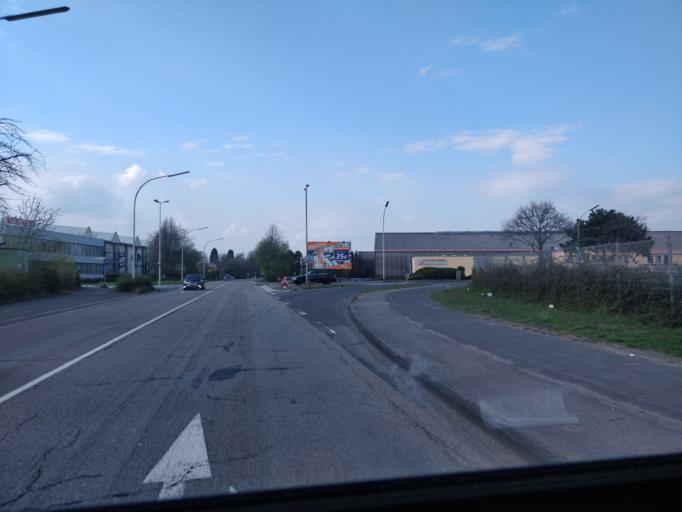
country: DE
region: North Rhine-Westphalia
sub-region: Regierungsbezirk Koln
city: Frechen
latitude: 50.9209
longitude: 6.8250
